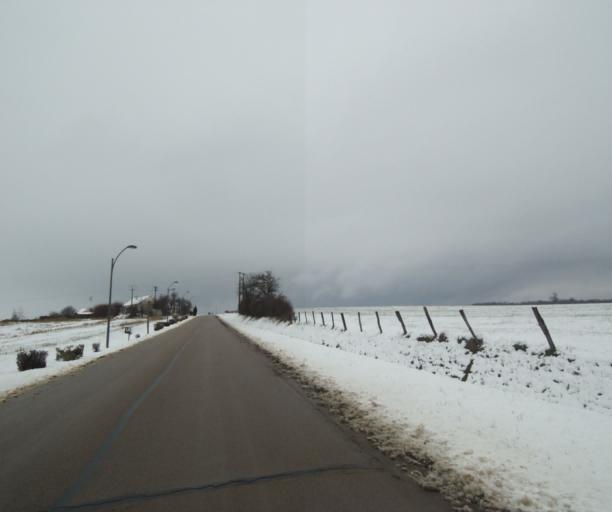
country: FR
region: Champagne-Ardenne
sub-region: Departement de la Haute-Marne
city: Laneuville-a-Remy
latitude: 48.4185
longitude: 4.8378
